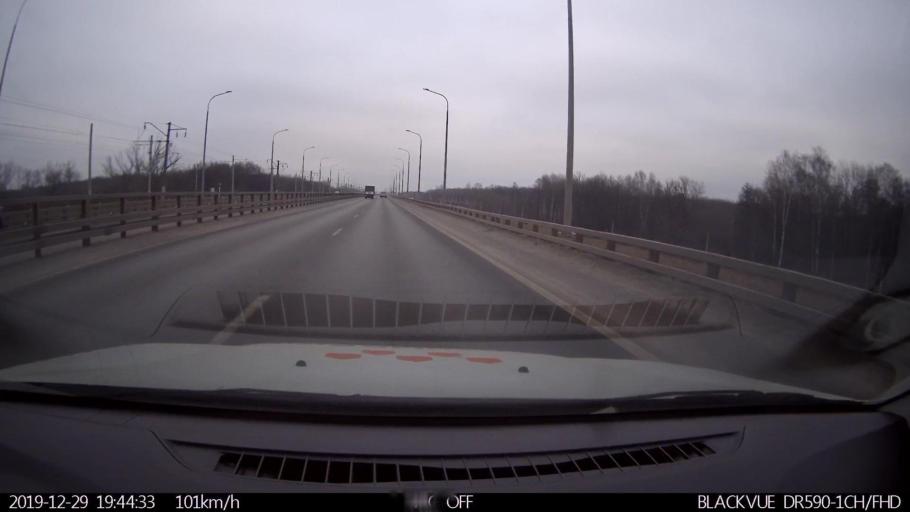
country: RU
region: Nizjnij Novgorod
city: Neklyudovo
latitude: 56.3759
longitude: 43.9529
